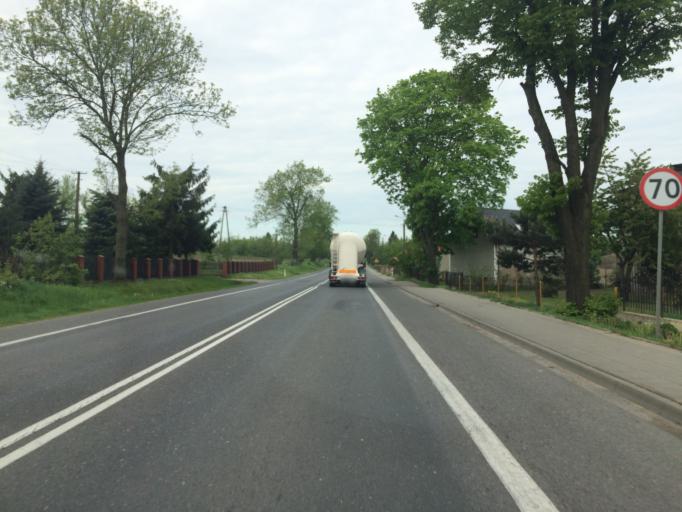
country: PL
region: Masovian Voivodeship
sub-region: Powiat mlawski
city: Mlawa
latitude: 53.0900
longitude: 20.3659
